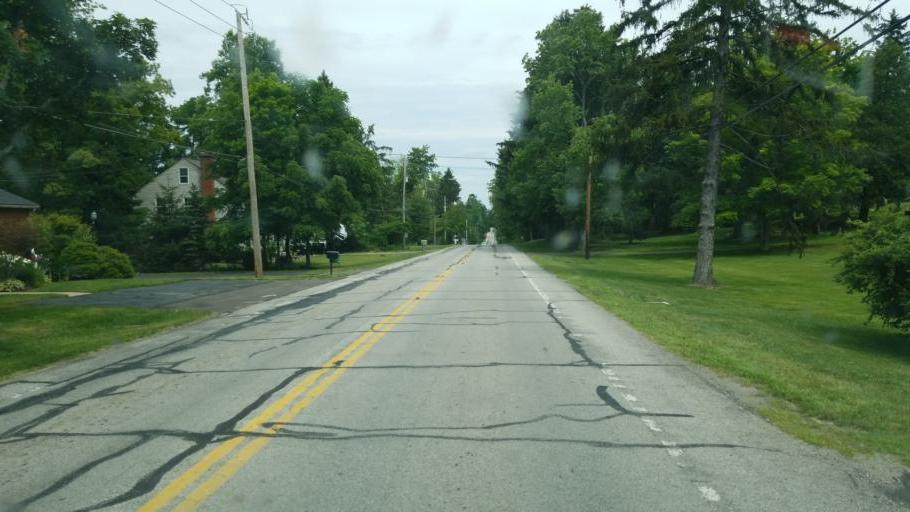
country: US
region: Ohio
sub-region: Geauga County
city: Bainbridge
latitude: 41.3875
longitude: -81.2462
